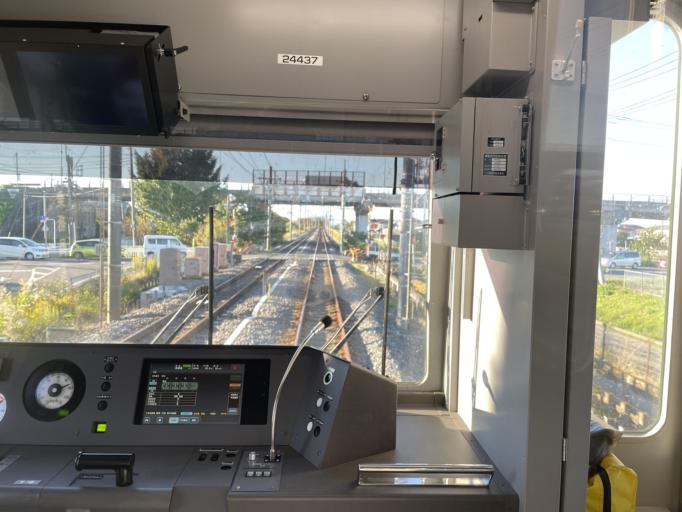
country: JP
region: Saitama
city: Kurihashi
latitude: 36.1268
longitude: 139.6969
